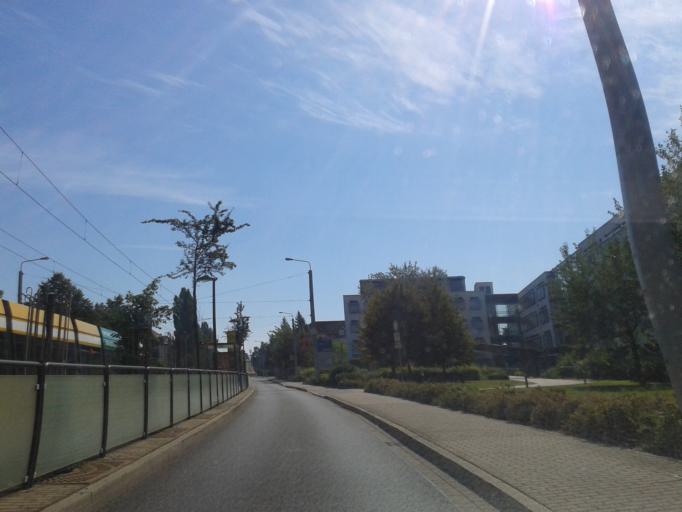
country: DE
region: Saxony
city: Dresden
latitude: 51.0285
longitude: 13.7940
